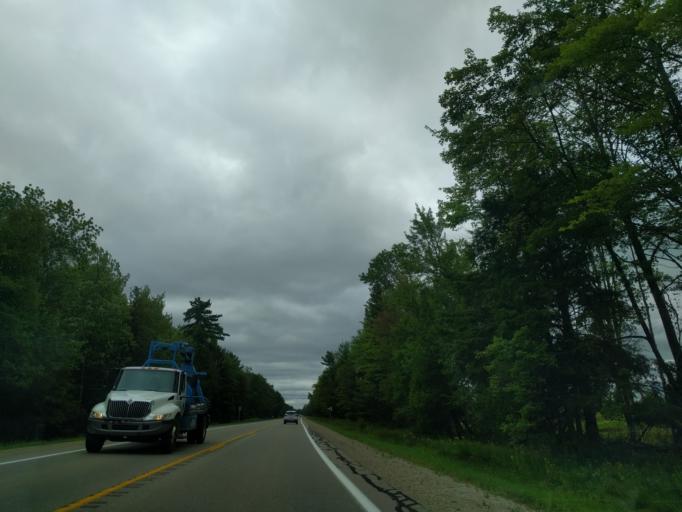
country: US
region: Michigan
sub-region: Delta County
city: Escanaba
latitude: 45.4713
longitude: -87.3127
